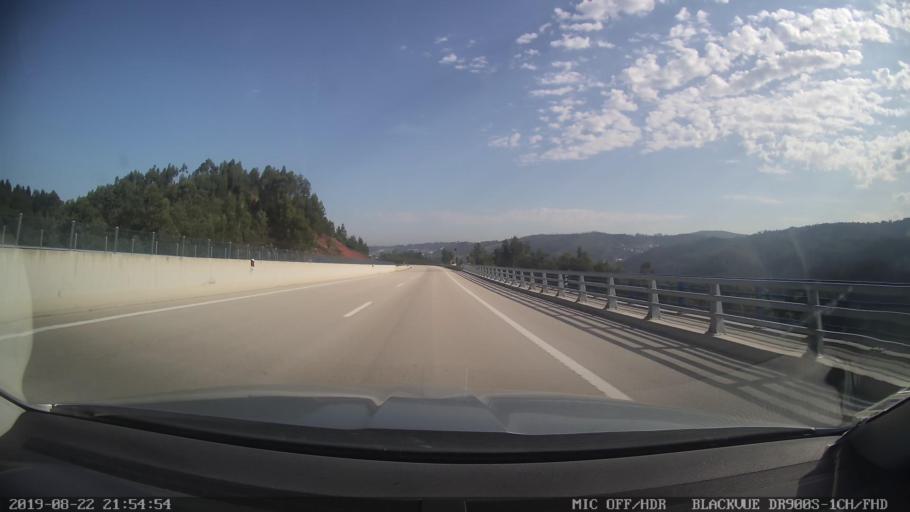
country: PT
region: Coimbra
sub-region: Miranda do Corvo
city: Miranda do Corvo
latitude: 40.1437
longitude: -8.3834
